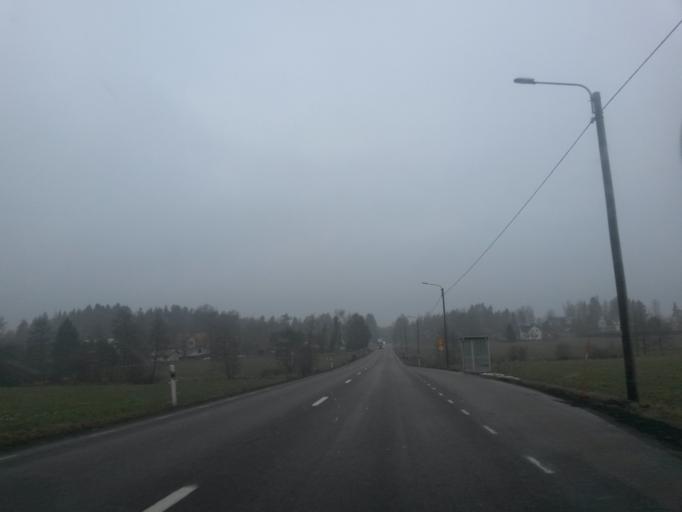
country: SE
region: Vaestra Goetaland
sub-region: Vanersborgs Kommun
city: Vargon
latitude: 58.2491
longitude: 12.4210
